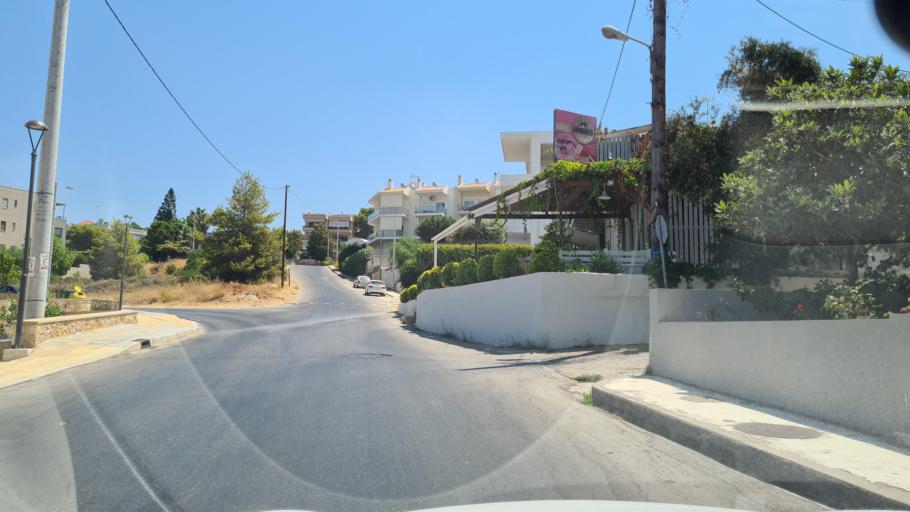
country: GR
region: Crete
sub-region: Nomos Chanias
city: Chania
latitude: 35.5202
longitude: 24.0485
